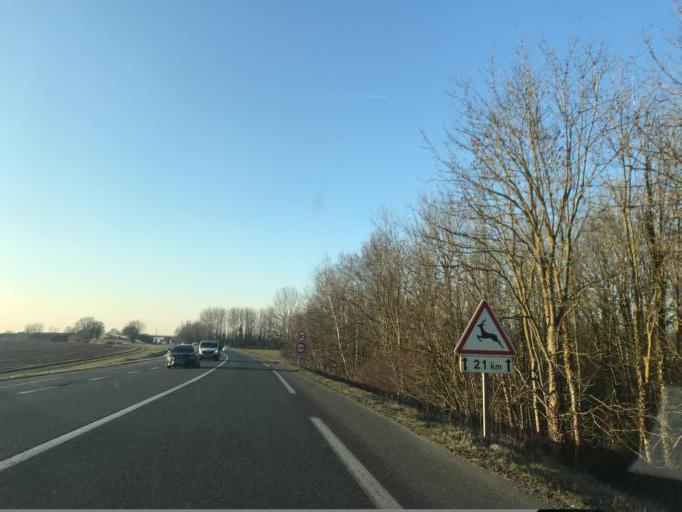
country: FR
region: Ile-de-France
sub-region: Departement de Seine-et-Marne
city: Villiers-sur-Morin
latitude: 48.8530
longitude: 2.8617
